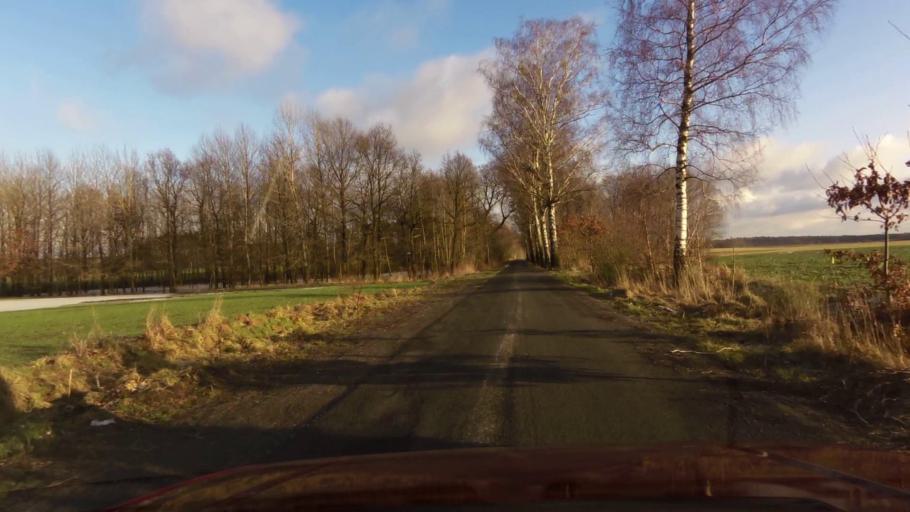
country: PL
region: West Pomeranian Voivodeship
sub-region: Koszalin
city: Koszalin
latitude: 54.0714
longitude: 16.1468
